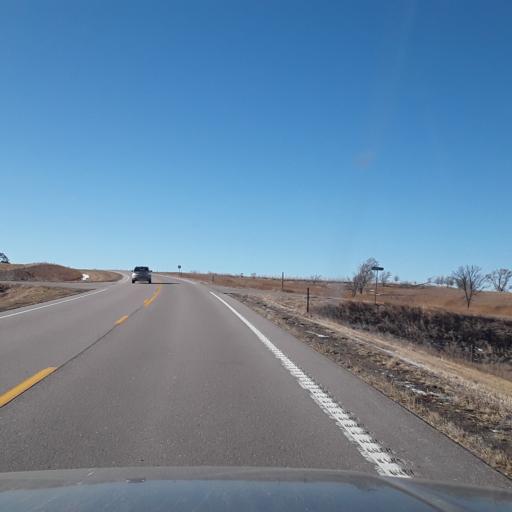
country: US
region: Nebraska
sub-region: Frontier County
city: Stockville
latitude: 40.7057
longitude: -100.2414
